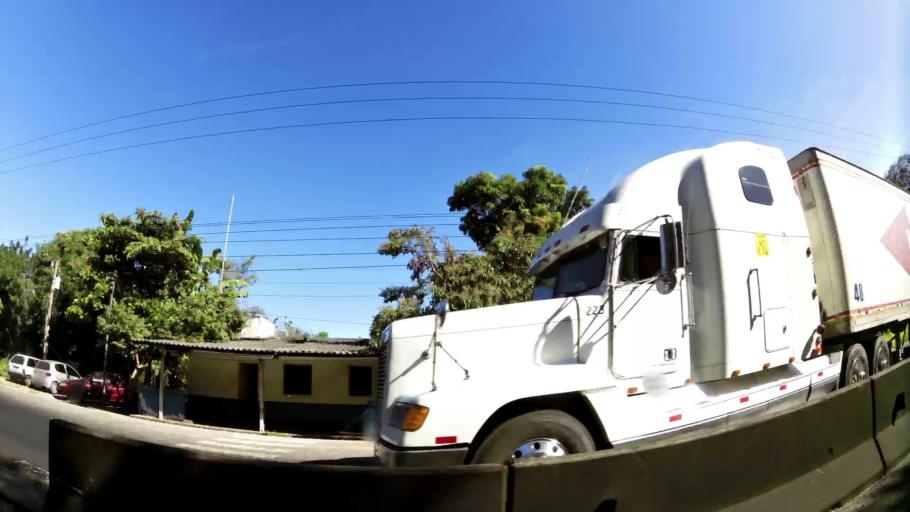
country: SV
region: Santa Ana
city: Santa Ana
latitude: 13.9545
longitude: -89.5630
